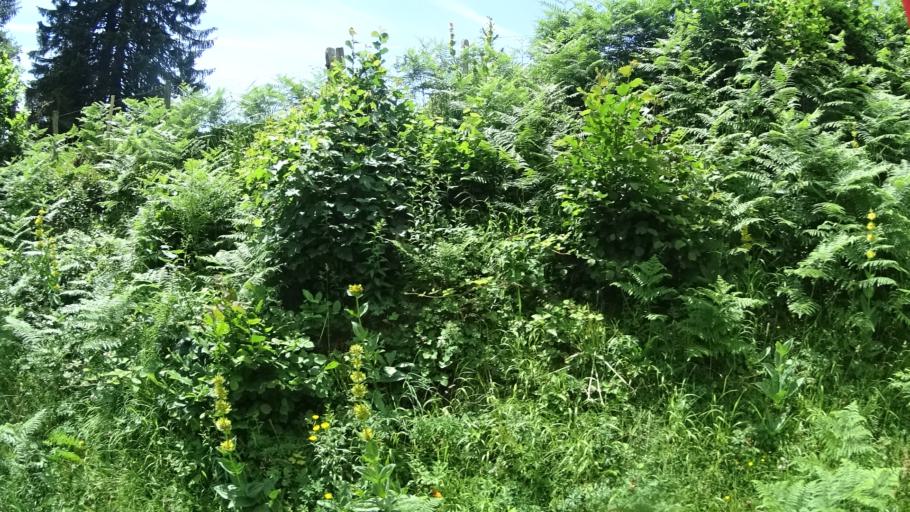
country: CH
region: Lucerne
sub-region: Lucerne-Land District
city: Vitznau
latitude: 47.0338
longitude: 8.4782
